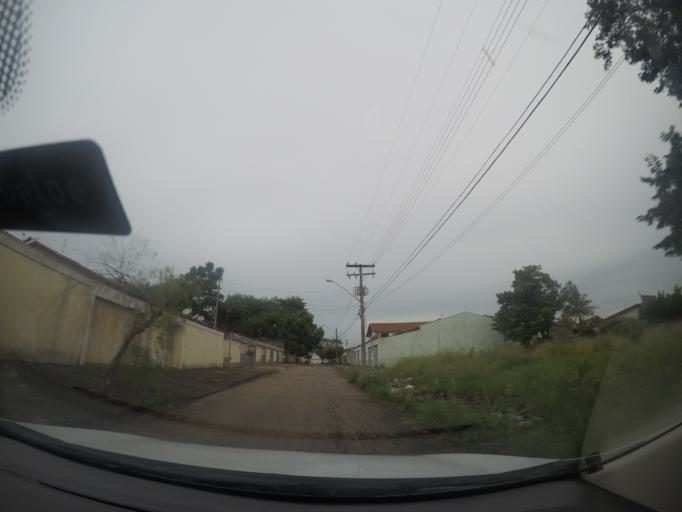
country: BR
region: Goias
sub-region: Goiania
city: Goiania
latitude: -16.6363
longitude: -49.2411
